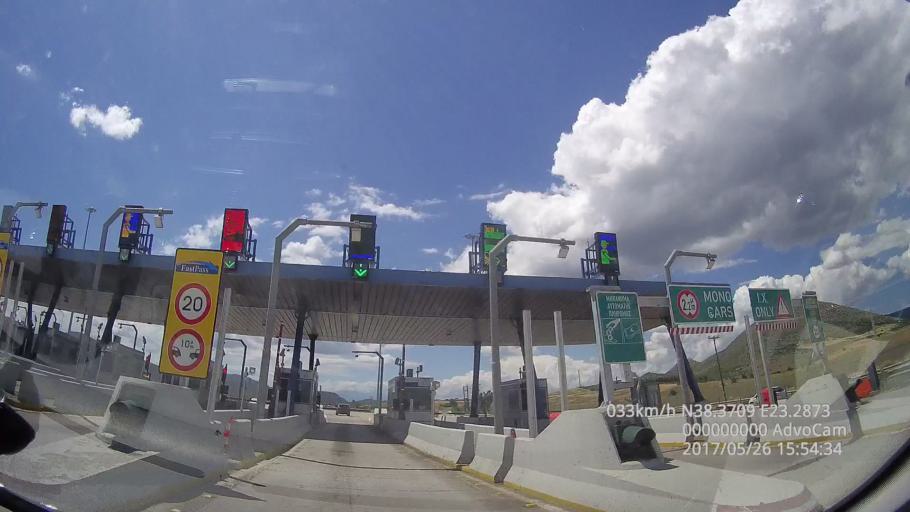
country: GR
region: Central Greece
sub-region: Nomos Fthiotidos
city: Ayios Konstandinos
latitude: 38.7510
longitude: 22.9119
